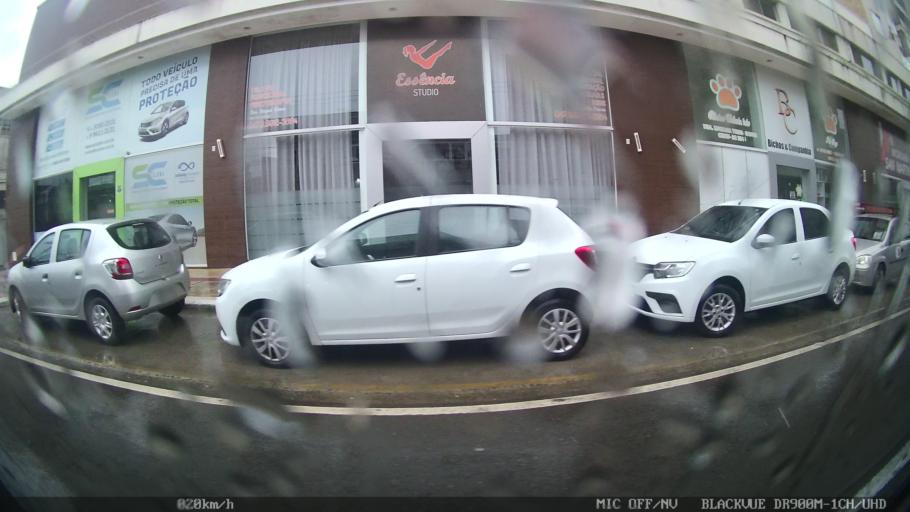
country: BR
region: Santa Catarina
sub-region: Balneario Camboriu
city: Balneario Camboriu
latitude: -27.0048
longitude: -48.6479
